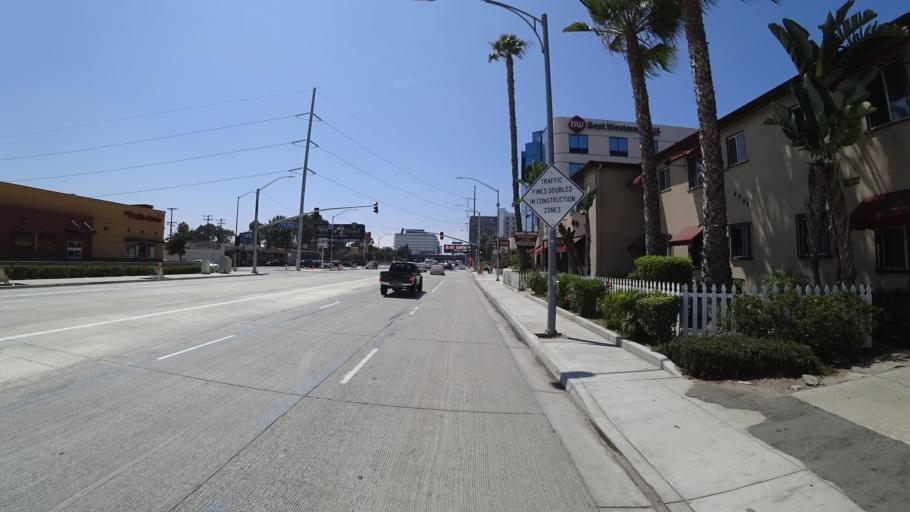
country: US
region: California
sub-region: Los Angeles County
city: Lennox
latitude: 33.9455
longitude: -118.3651
